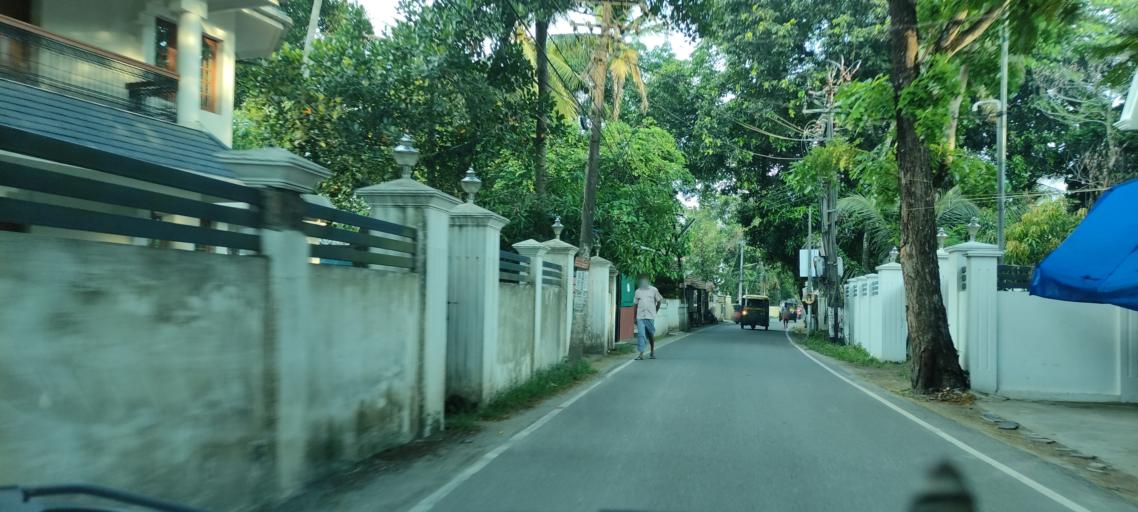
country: IN
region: Kerala
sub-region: Alappuzha
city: Arukutti
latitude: 9.8932
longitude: 76.3109
